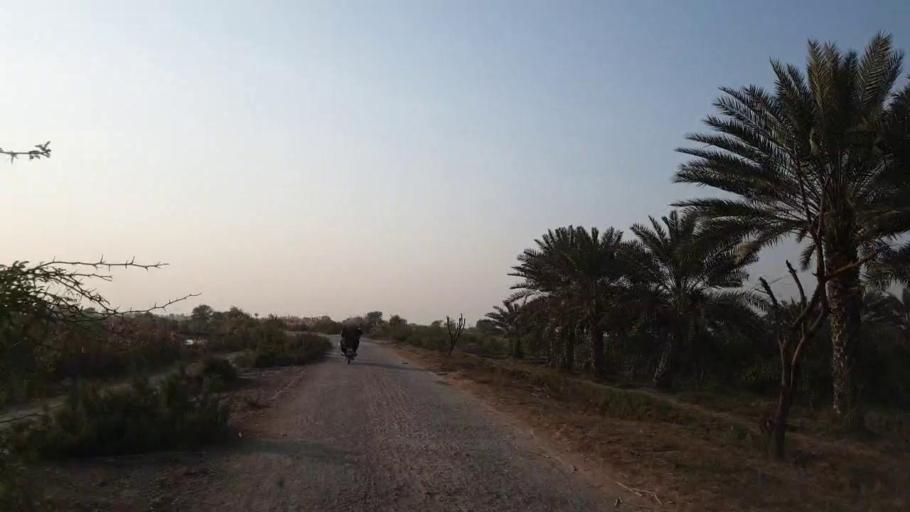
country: PK
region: Sindh
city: Pithoro
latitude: 25.6536
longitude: 69.2323
